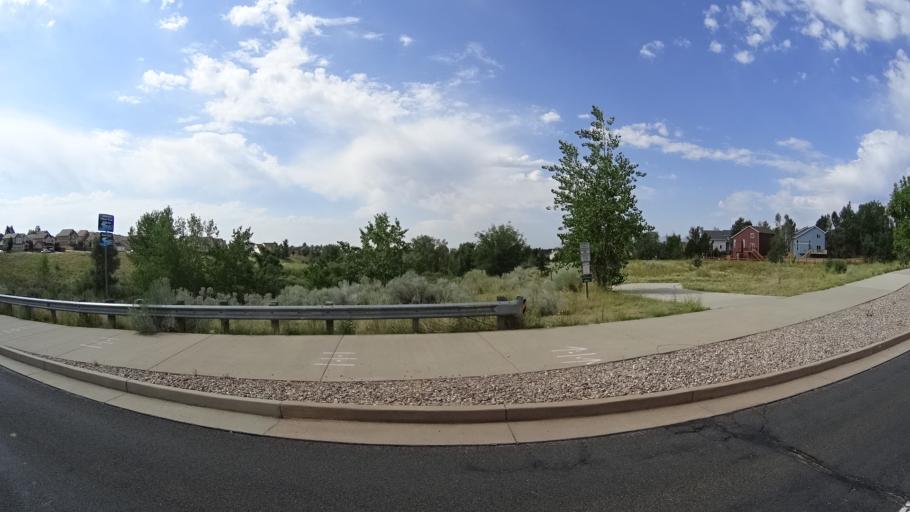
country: US
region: Colorado
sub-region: El Paso County
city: Cimarron Hills
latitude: 38.9120
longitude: -104.7022
